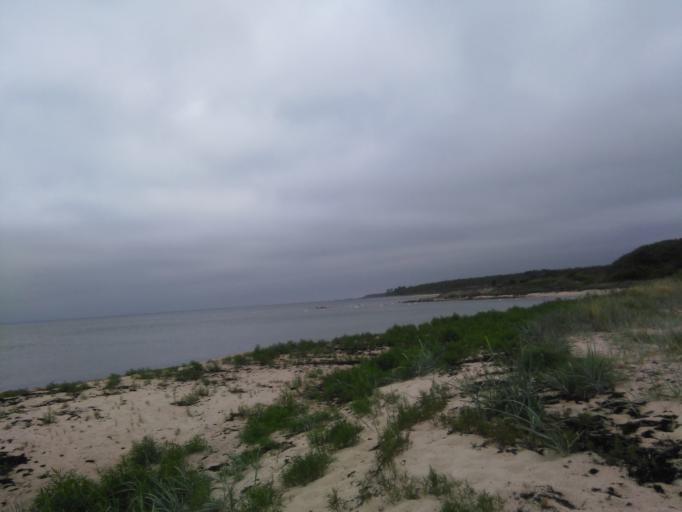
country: DK
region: Capital Region
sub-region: Bornholm Kommune
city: Ronne
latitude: 55.1485
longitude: 14.7044
